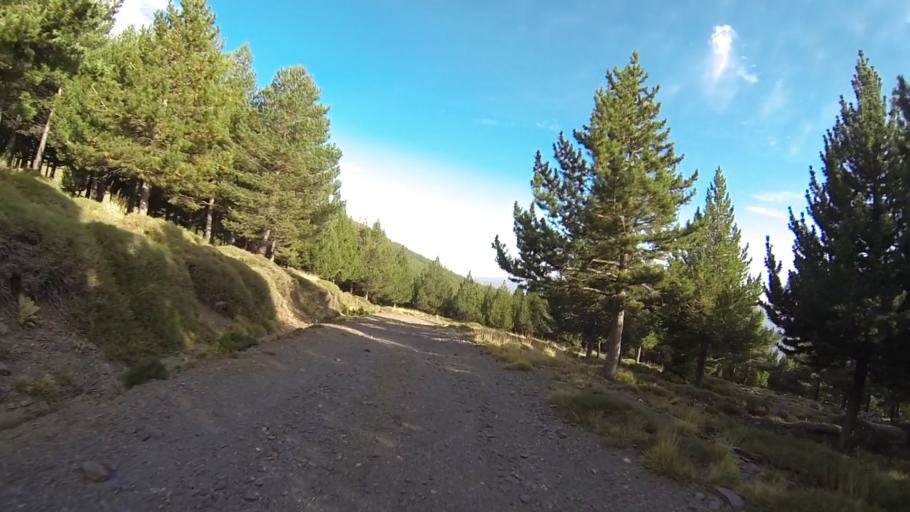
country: ES
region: Andalusia
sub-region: Provincia de Almeria
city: Paterna del Rio
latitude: 37.0827
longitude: -2.9026
